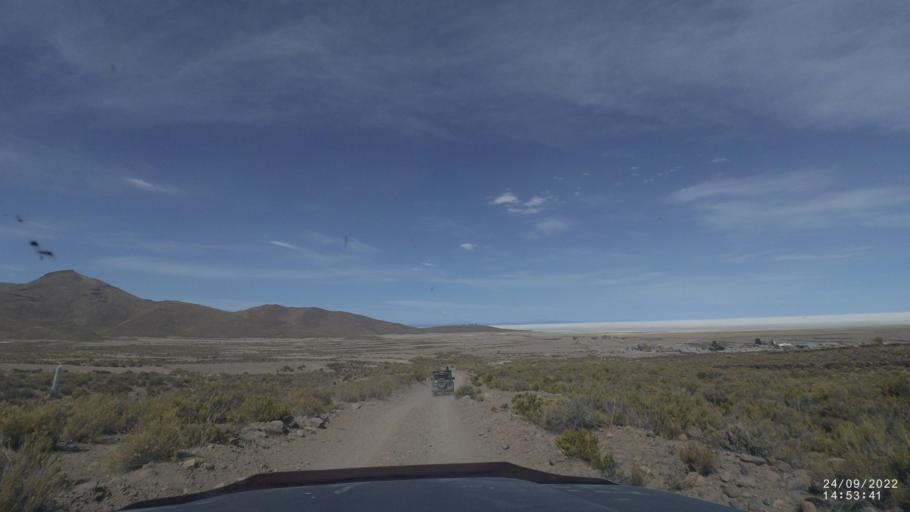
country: BO
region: Potosi
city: Colchani
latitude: -19.8528
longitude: -67.5781
